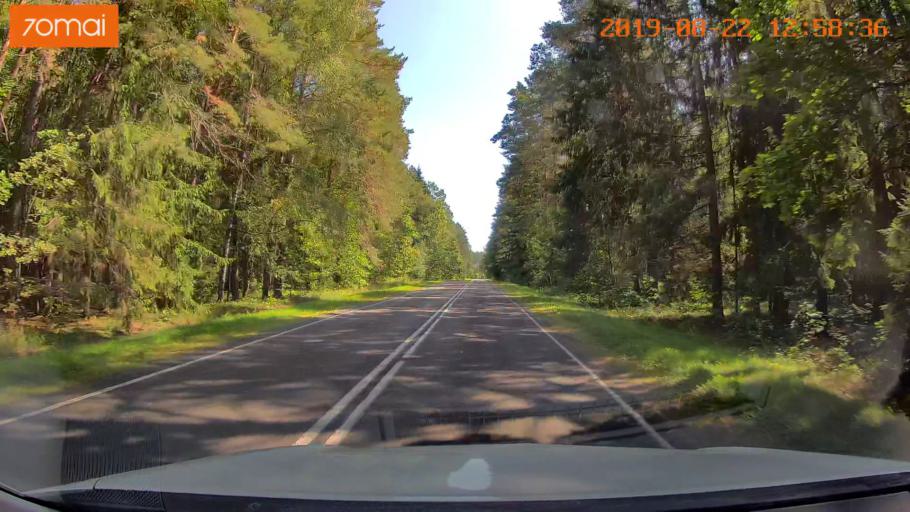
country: BY
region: Minsk
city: Prawdzinski
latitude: 53.4232
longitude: 27.7742
